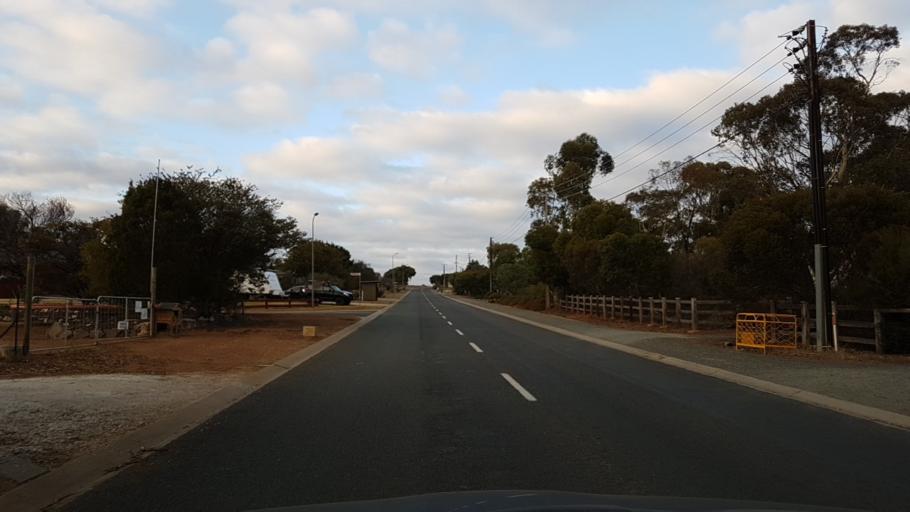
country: AU
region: South Australia
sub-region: Mount Barker
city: Callington
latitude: -35.0779
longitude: 139.0128
